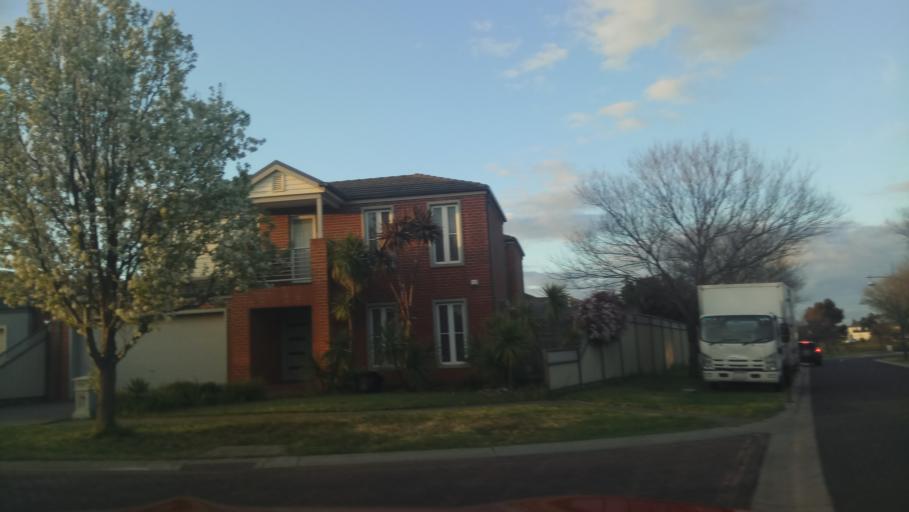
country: AU
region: Victoria
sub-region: Wyndham
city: Point Cook
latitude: -37.8972
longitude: 144.7412
